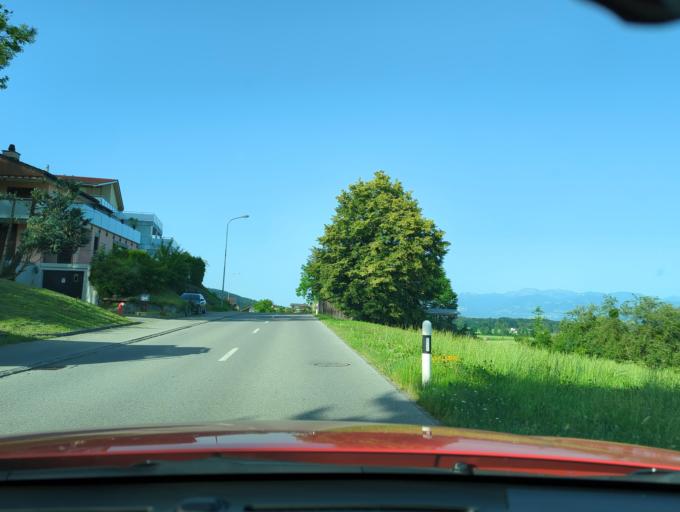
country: CH
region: Saint Gallen
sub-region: Wahlkreis Werdenberg
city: Gams
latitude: 47.2358
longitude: 9.4612
